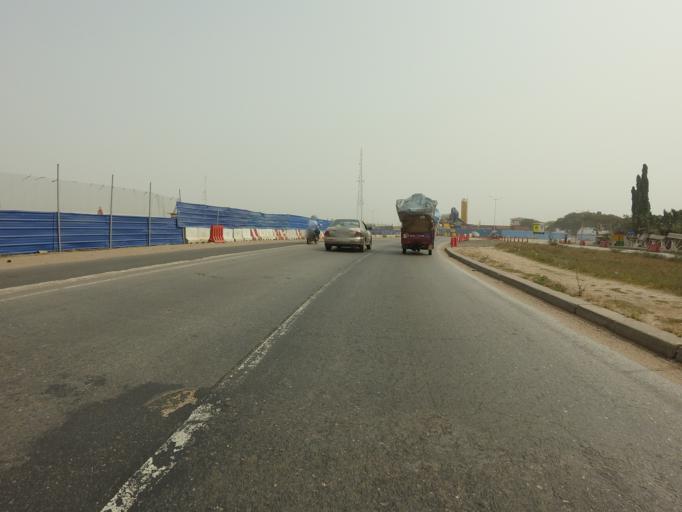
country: GH
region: Greater Accra
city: Tema
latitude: 5.6851
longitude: -0.0160
